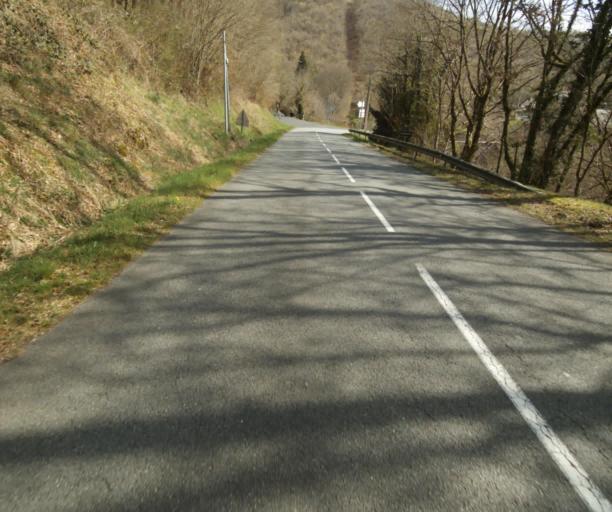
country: FR
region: Limousin
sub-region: Departement de la Correze
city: Naves
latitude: 45.3387
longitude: 1.7916
